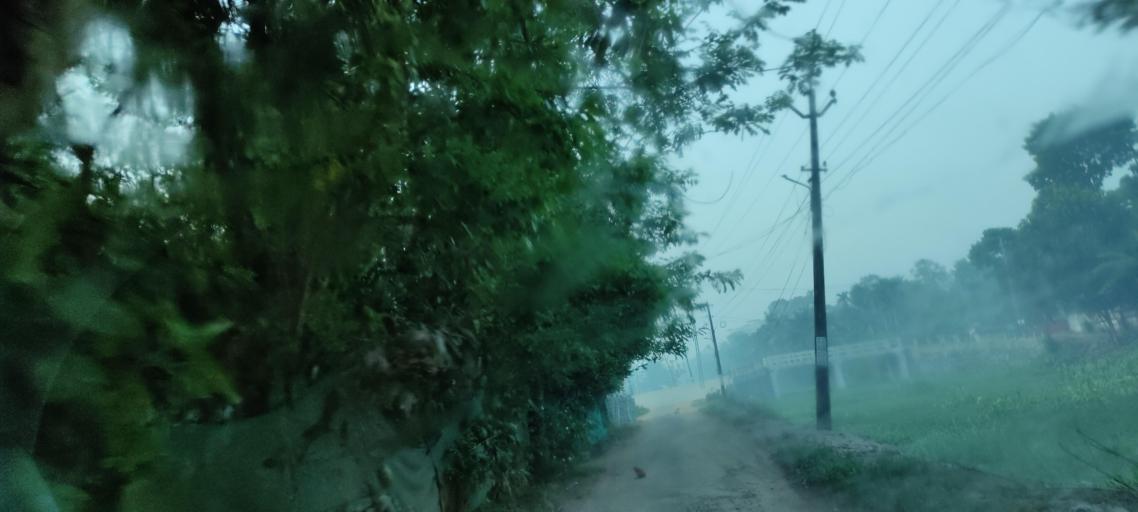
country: IN
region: Kerala
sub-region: Alappuzha
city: Alleppey
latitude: 9.5297
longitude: 76.3293
